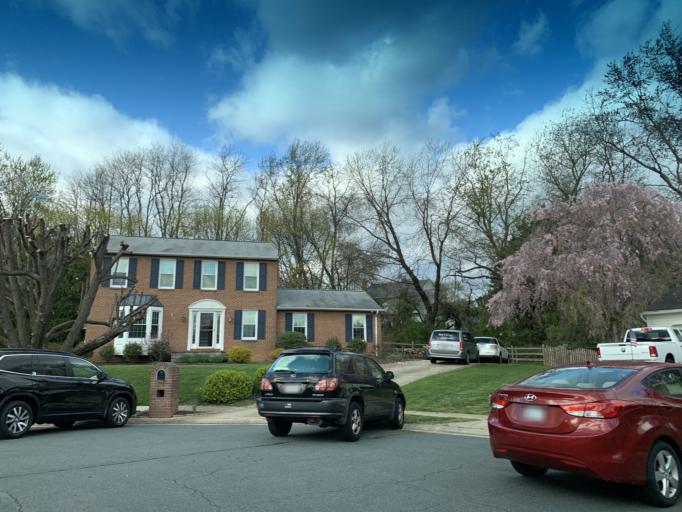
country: US
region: Maryland
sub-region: Harford County
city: South Bel Air
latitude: 39.5468
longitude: -76.3215
